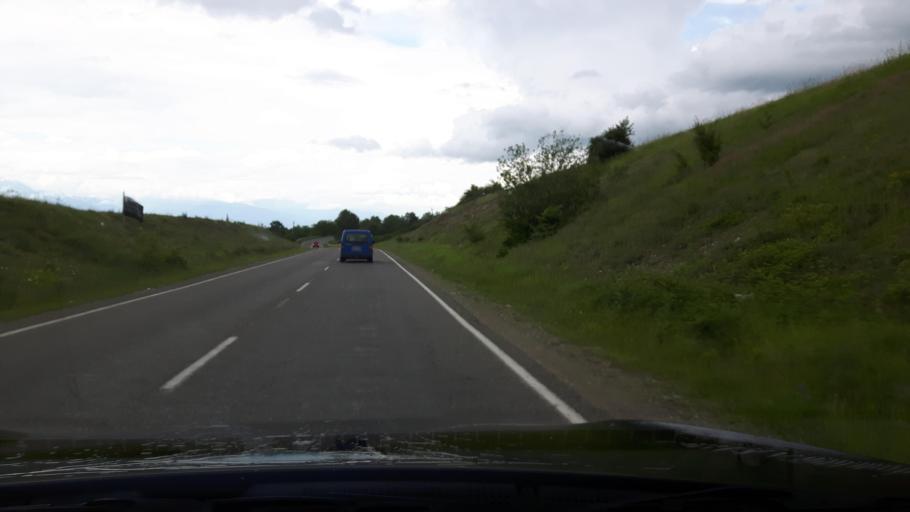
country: GE
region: Kakheti
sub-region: Telavi
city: Telavi
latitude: 41.9286
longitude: 45.4257
